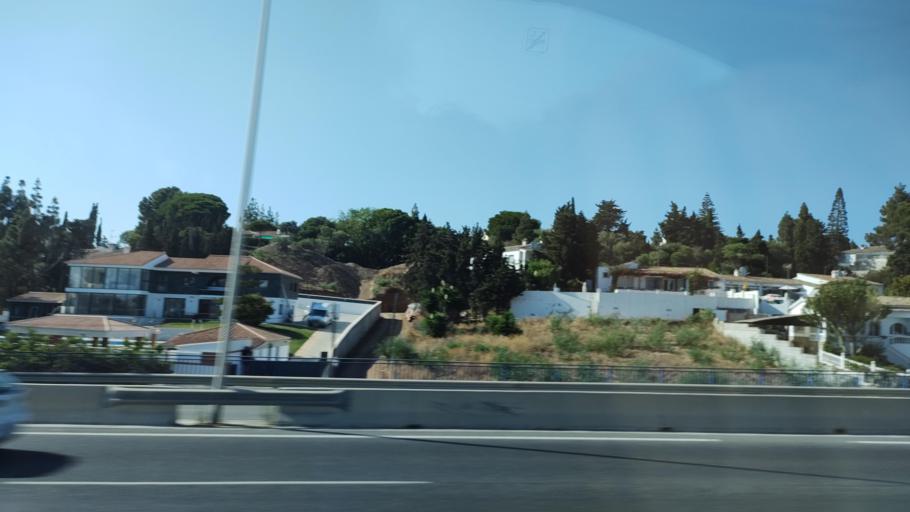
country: ES
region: Andalusia
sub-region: Provincia de Malaga
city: Fuengirola
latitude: 36.5070
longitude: -4.6639
